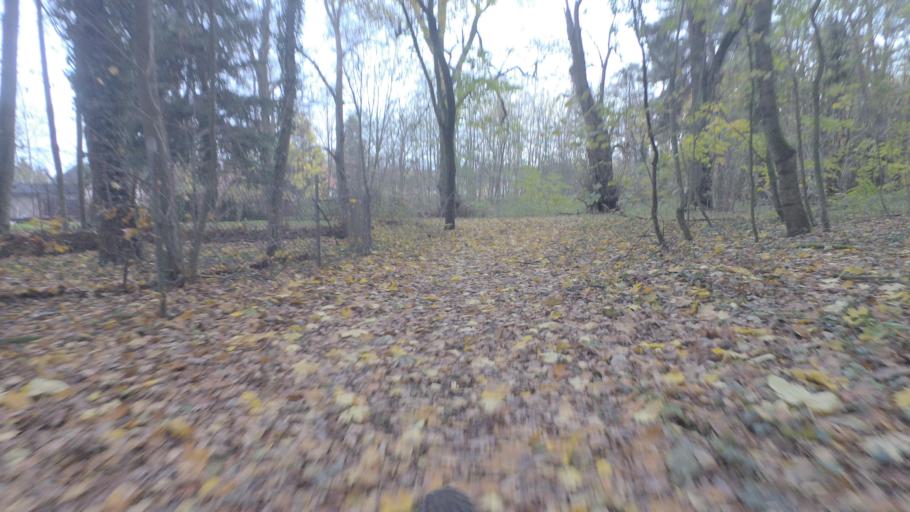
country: DE
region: Brandenburg
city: Rangsdorf
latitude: 52.3010
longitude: 13.4218
